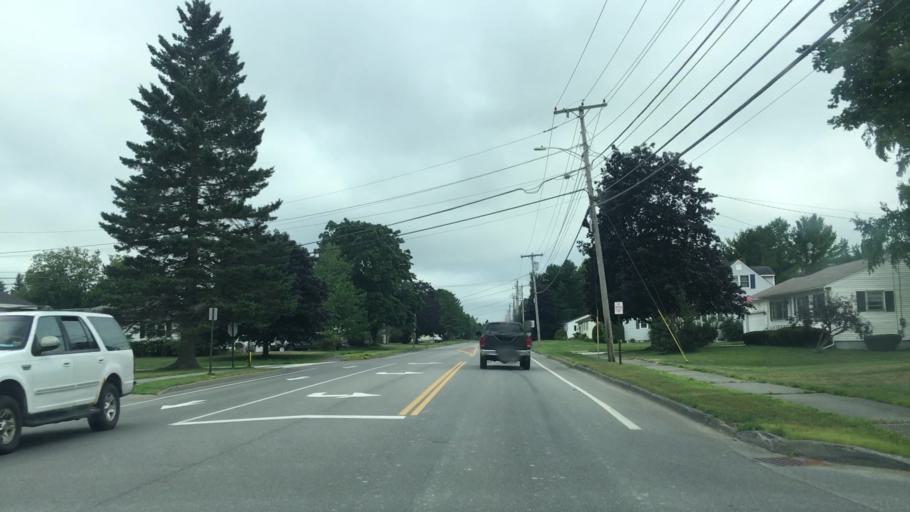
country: US
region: Maine
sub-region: Penobscot County
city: Brewer
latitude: 44.7750
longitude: -68.7699
